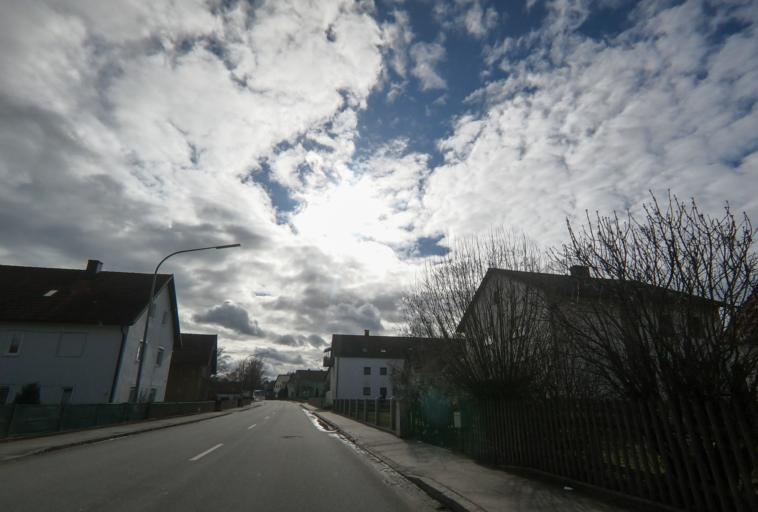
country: DE
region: Bavaria
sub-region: Lower Bavaria
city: Ergoldsbach
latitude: 48.7007
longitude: 12.2011
